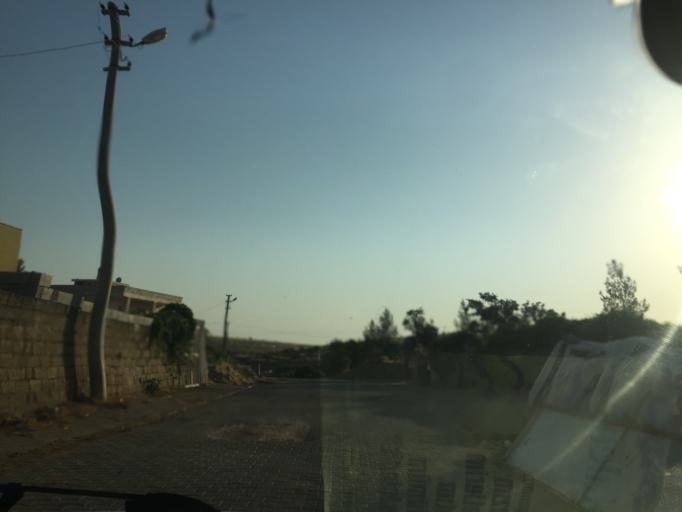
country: TR
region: Mardin
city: Kindirip
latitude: 37.4435
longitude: 41.2146
